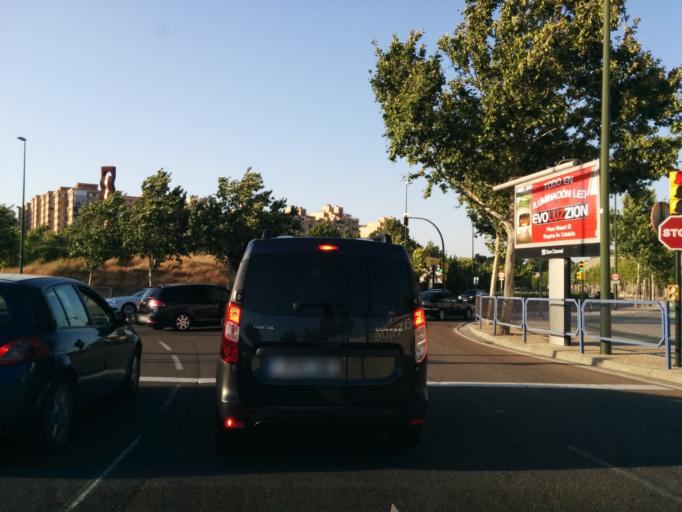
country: ES
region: Aragon
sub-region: Provincia de Zaragoza
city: Zaragoza
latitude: 41.6206
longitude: -0.8758
